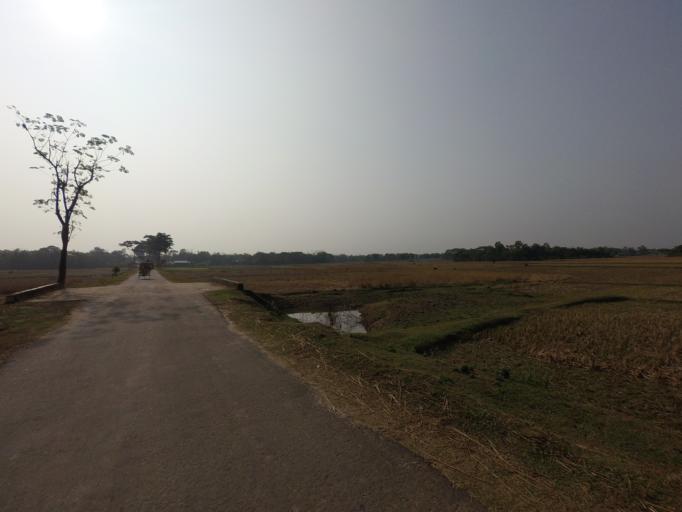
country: BD
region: Dhaka
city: Netrakona
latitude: 25.0918
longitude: 90.6829
